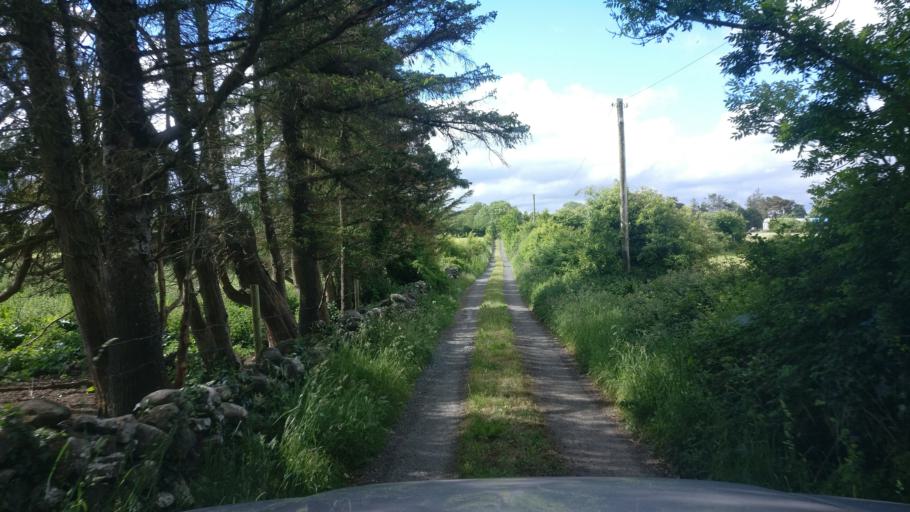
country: IE
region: Connaught
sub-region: County Galway
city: Loughrea
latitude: 53.2399
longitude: -8.6018
